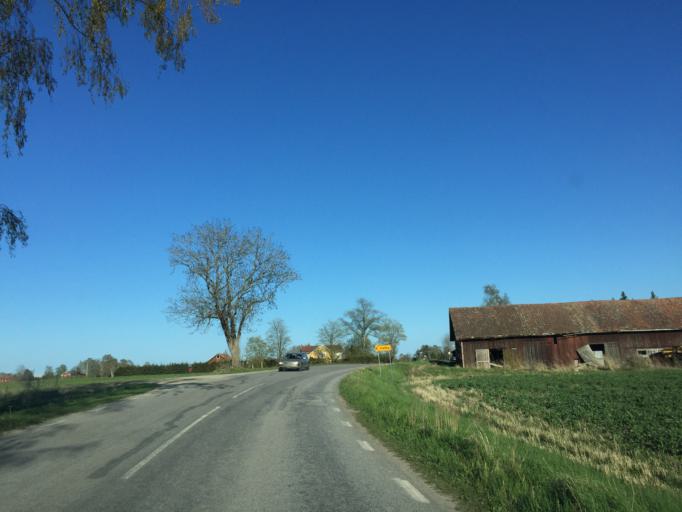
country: SE
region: OErebro
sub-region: Orebro Kommun
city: Odensbacken
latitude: 59.2051
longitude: 15.5189
